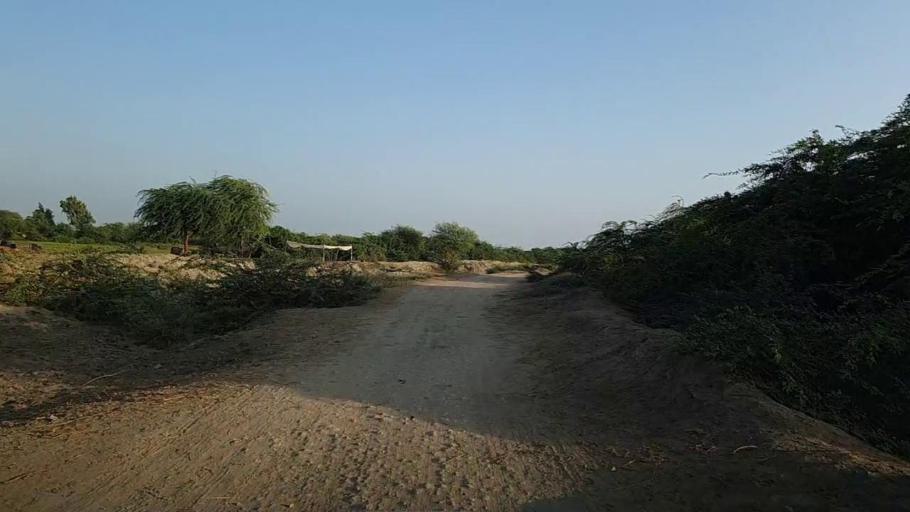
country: PK
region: Sindh
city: Kario
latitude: 24.7027
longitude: 68.6697
